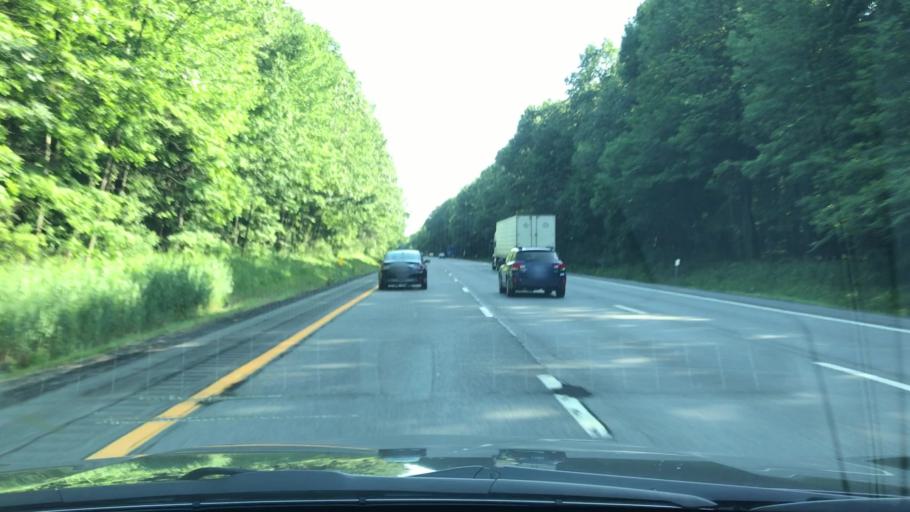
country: US
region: New York
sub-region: Warren County
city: West Glens Falls
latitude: 43.1838
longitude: -73.7076
